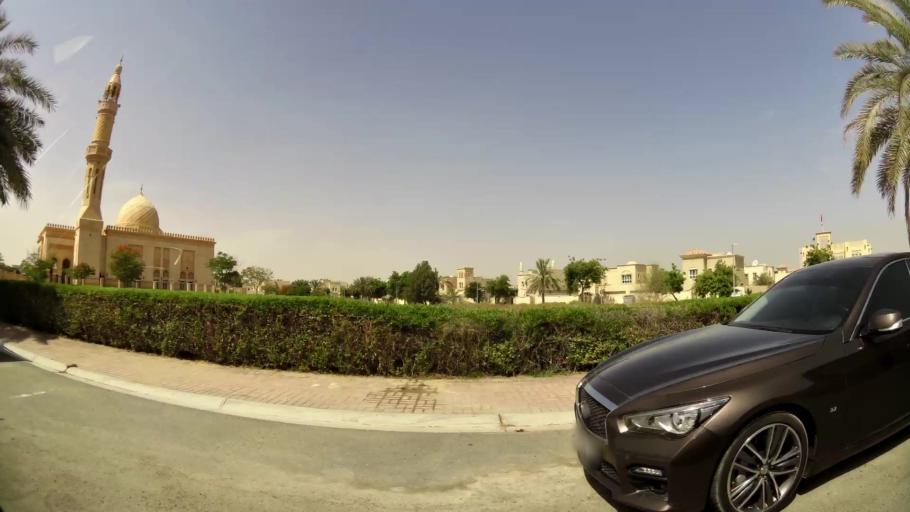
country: AE
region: Ash Shariqah
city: Sharjah
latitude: 25.1886
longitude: 55.4424
